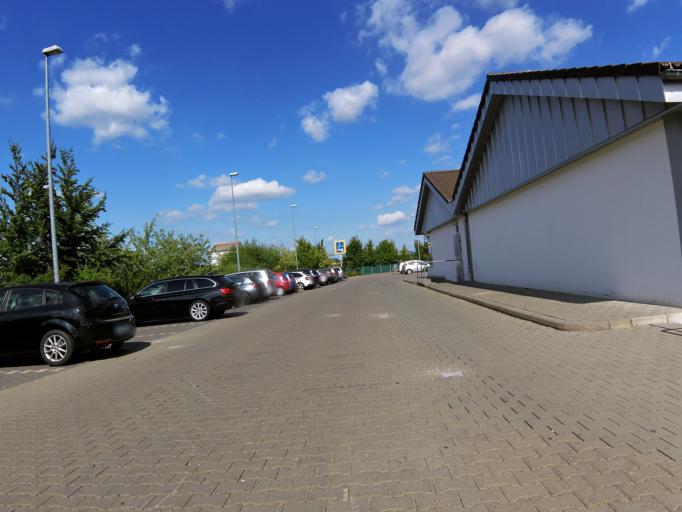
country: DE
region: Bavaria
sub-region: Regierungsbezirk Unterfranken
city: Gerbrunn
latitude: 49.7876
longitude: 9.9901
